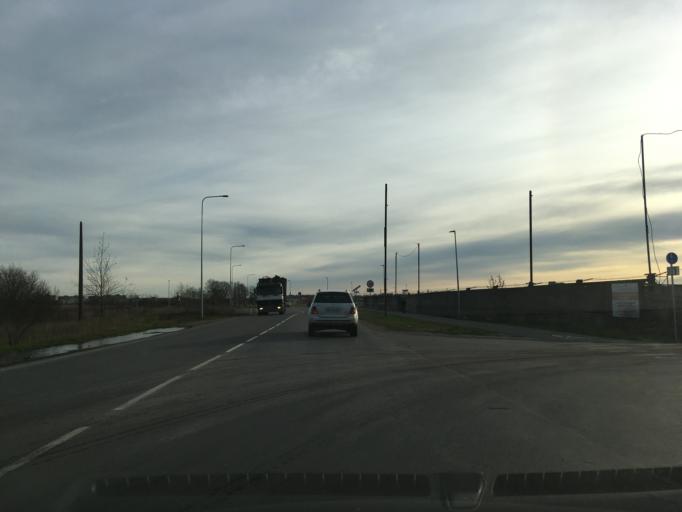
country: EE
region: Ida-Virumaa
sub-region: Narva linn
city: Narva
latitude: 59.3685
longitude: 28.1570
